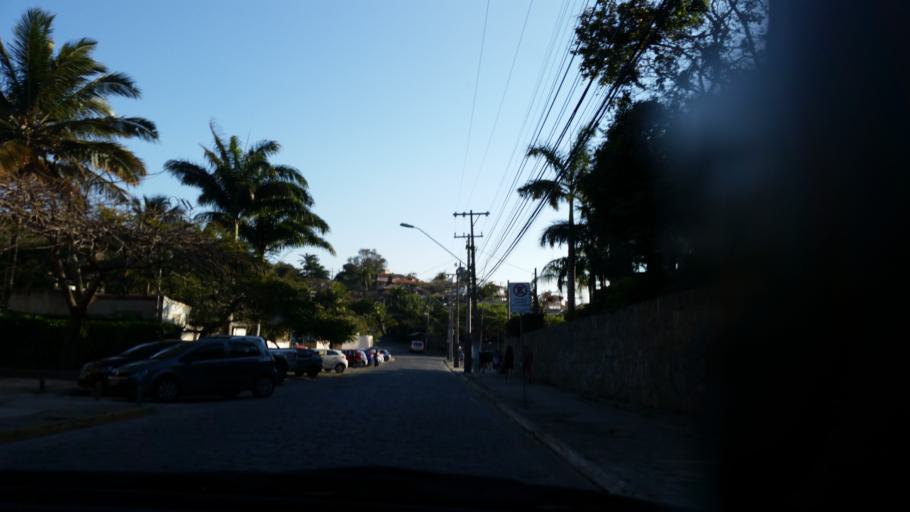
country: BR
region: Rio de Janeiro
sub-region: Armacao De Buzios
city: Armacao de Buzios
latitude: -22.7461
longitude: -41.8784
